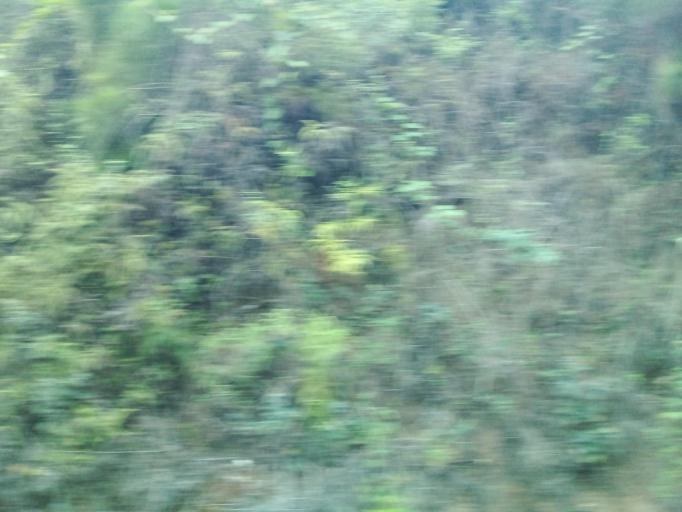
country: BR
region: Minas Gerais
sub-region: Nova Era
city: Nova Era
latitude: -19.7324
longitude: -42.9830
